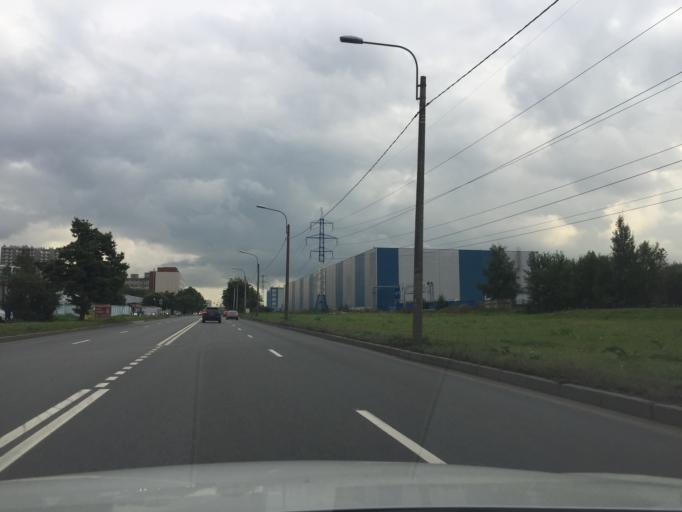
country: RU
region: St.-Petersburg
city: Dachnoye
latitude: 59.8449
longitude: 30.2941
